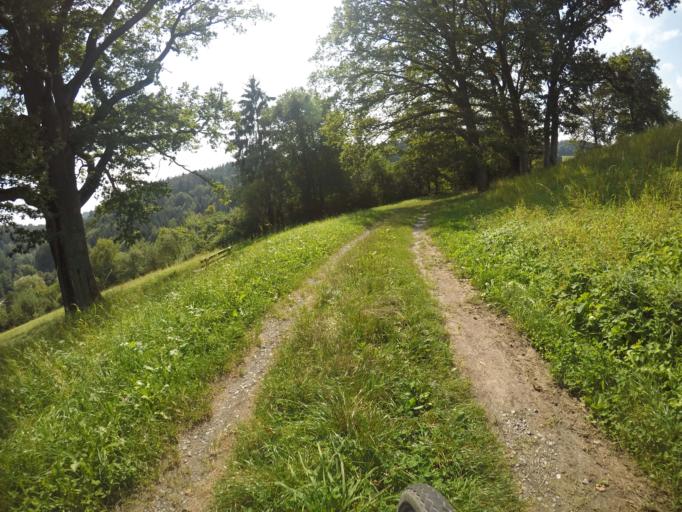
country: DE
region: Baden-Wuerttemberg
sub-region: Regierungsbezirk Stuttgart
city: Steinenbronn
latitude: 48.6864
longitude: 9.1274
